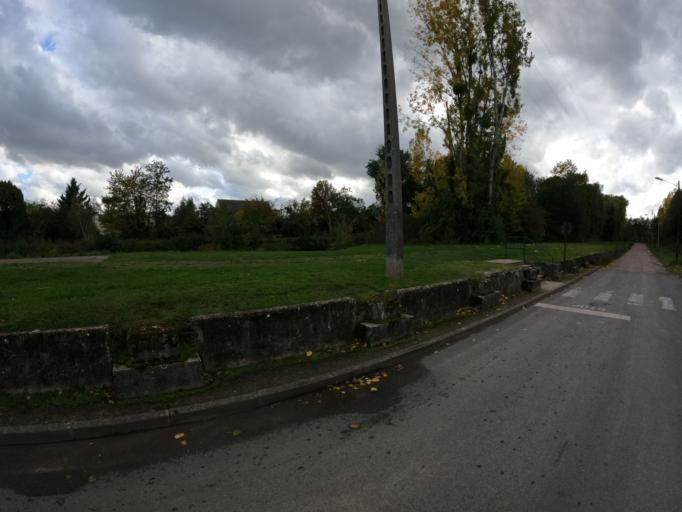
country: FR
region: Ile-de-France
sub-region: Departement de Seine-et-Marne
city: Esbly
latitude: 48.8991
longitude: 2.8086
